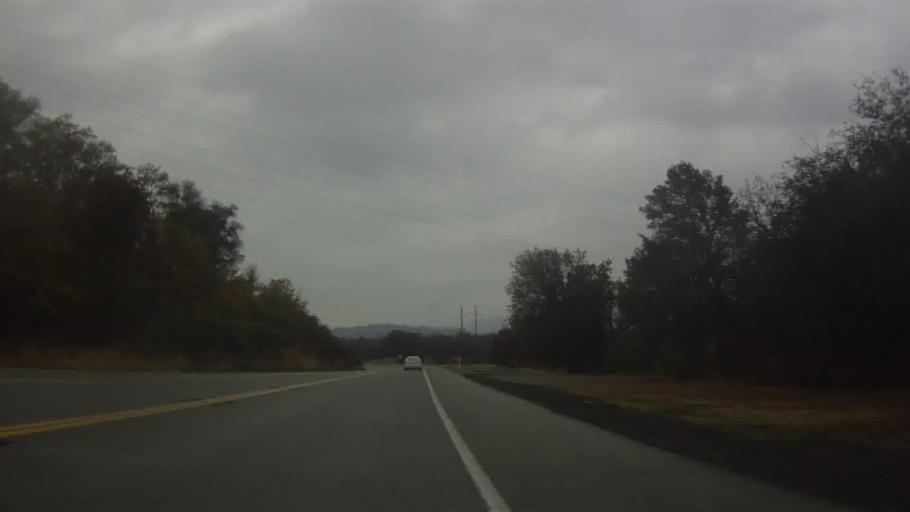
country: US
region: California
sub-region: Shasta County
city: Redding
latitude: 40.5825
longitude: -122.4377
